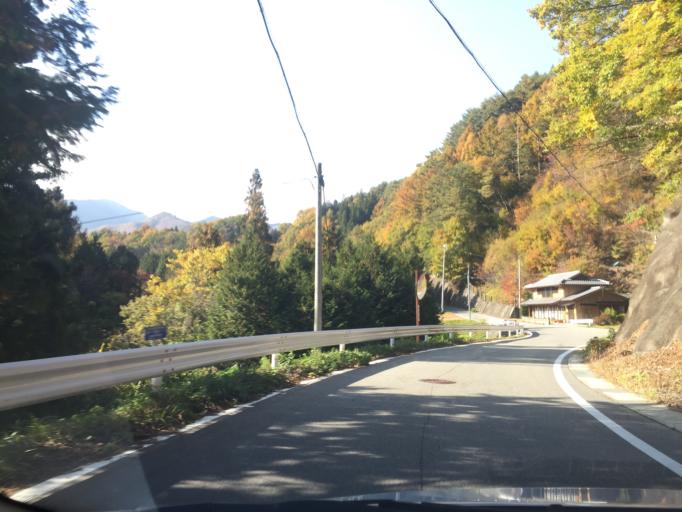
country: JP
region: Nagano
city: Iida
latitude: 35.3723
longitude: 137.7024
